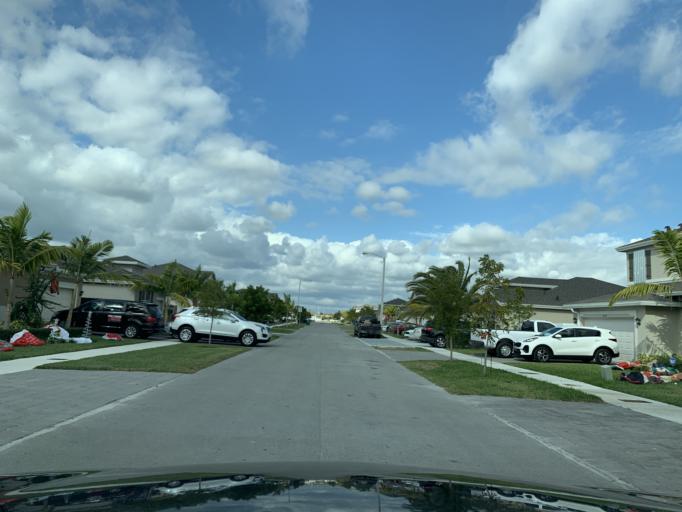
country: US
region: Florida
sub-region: Miami-Dade County
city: Naranja
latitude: 25.5094
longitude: -80.4082
